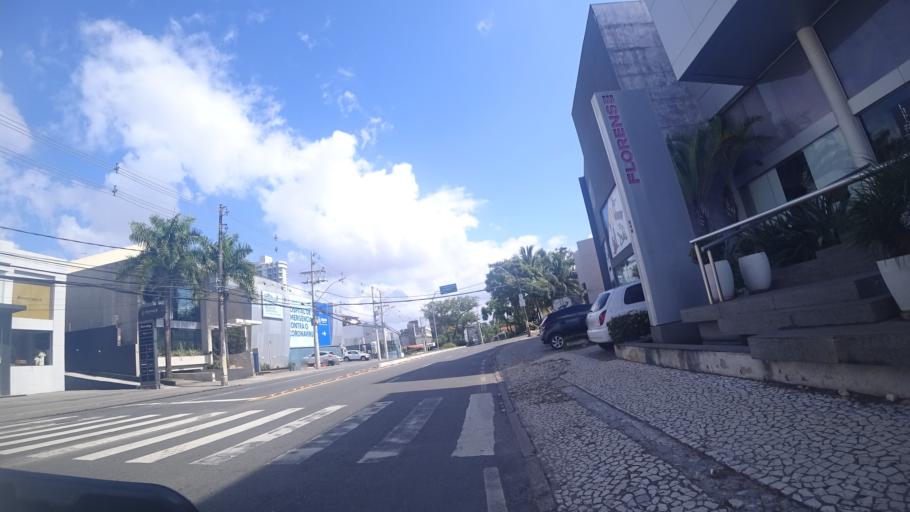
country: BR
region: Bahia
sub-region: Salvador
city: Salvador
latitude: -12.9826
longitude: -38.4585
